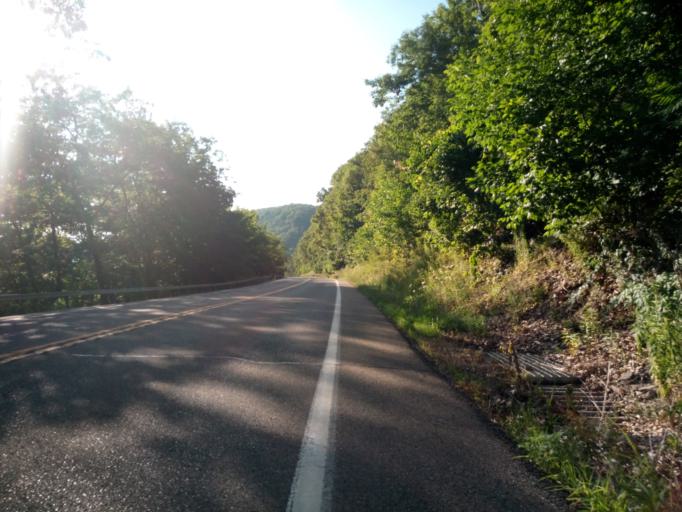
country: US
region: New York
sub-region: Chemung County
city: West Elmira
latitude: 42.0912
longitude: -76.8729
